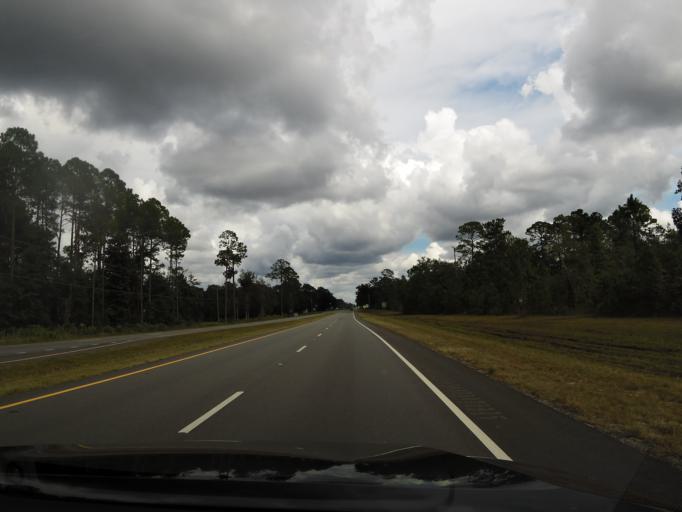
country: US
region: Georgia
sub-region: Brantley County
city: Nahunta
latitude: 31.2285
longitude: -81.7966
